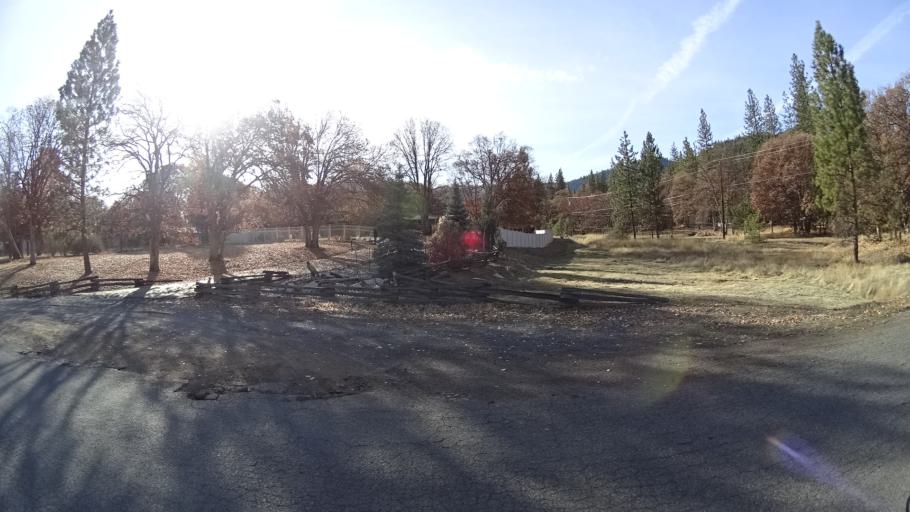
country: US
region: California
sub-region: Siskiyou County
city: Yreka
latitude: 41.6766
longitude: -122.6374
